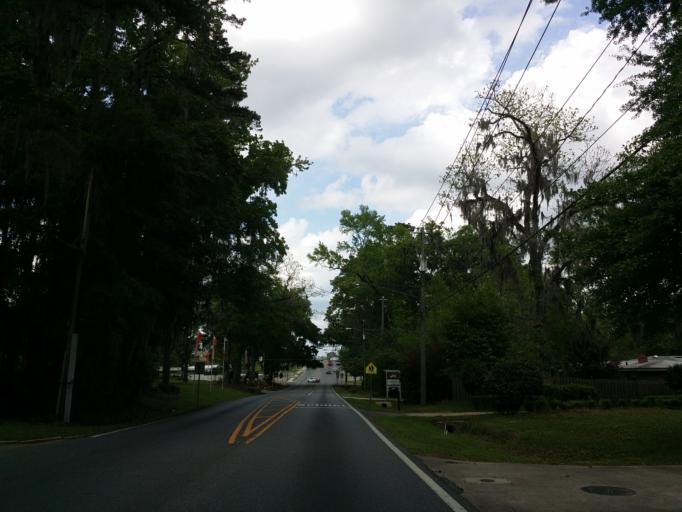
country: US
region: Florida
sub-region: Leon County
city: Tallahassee
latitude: 30.4328
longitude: -84.2618
